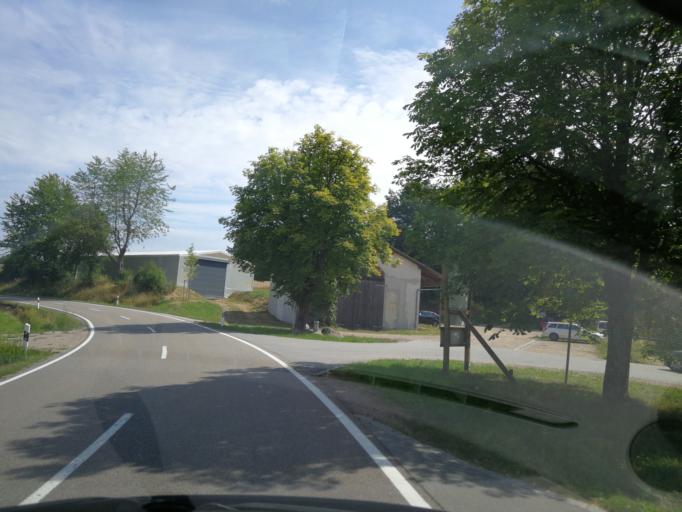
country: DE
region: Bavaria
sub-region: Lower Bavaria
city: Wiesenfelden
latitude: 49.0415
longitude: 12.5428
